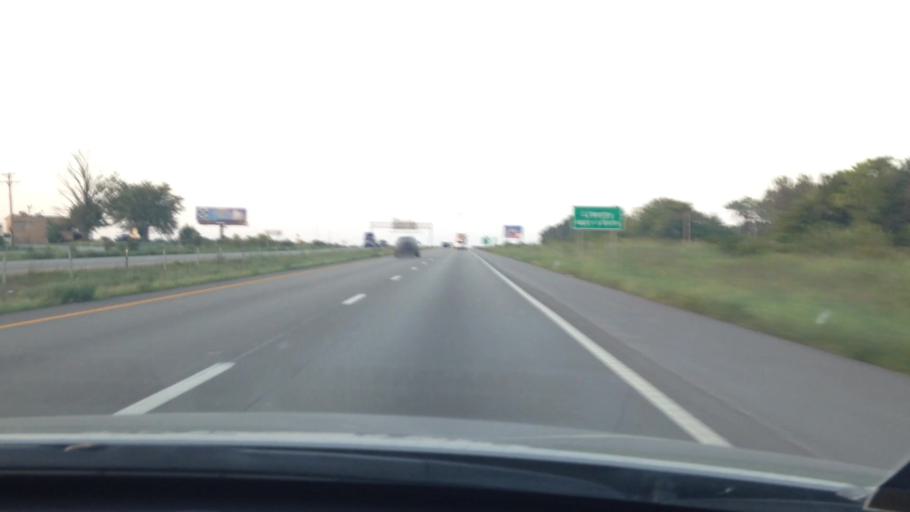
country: US
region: Missouri
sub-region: Clay County
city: Pleasant Valley
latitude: 39.2292
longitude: -94.4664
